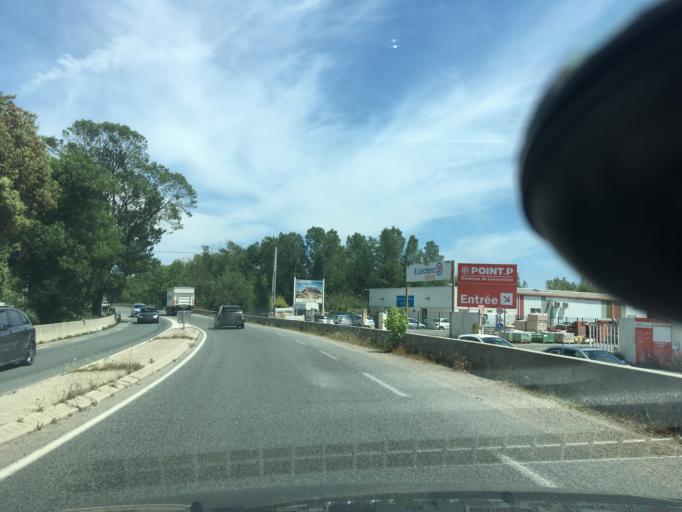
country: FR
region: Provence-Alpes-Cote d'Azur
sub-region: Departement du Var
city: Roquebrune-sur-Argens
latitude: 43.4623
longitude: 6.6449
